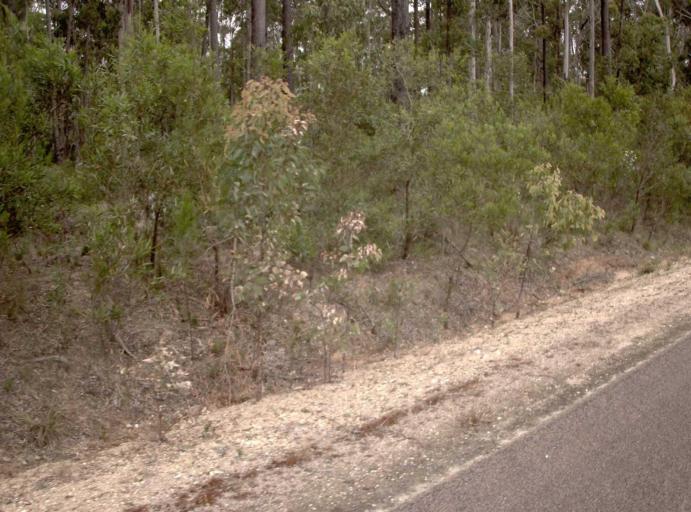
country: AU
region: Victoria
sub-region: East Gippsland
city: Lakes Entrance
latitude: -37.7104
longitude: 148.0717
